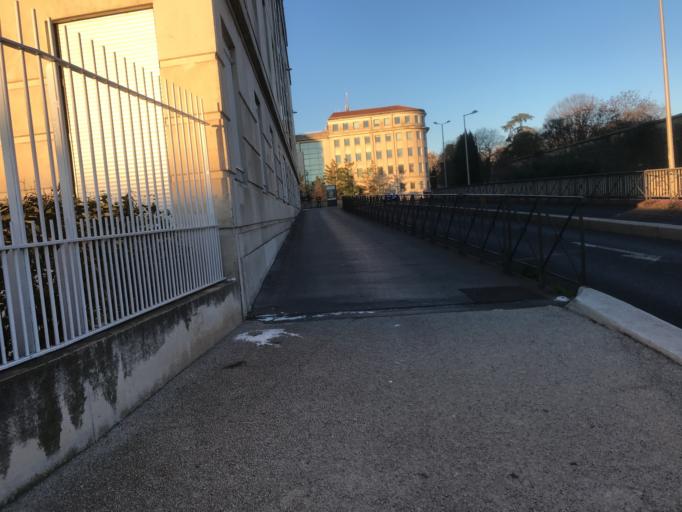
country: FR
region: Languedoc-Roussillon
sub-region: Departement de l'Herault
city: Montpellier
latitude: 43.6102
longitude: 3.8847
